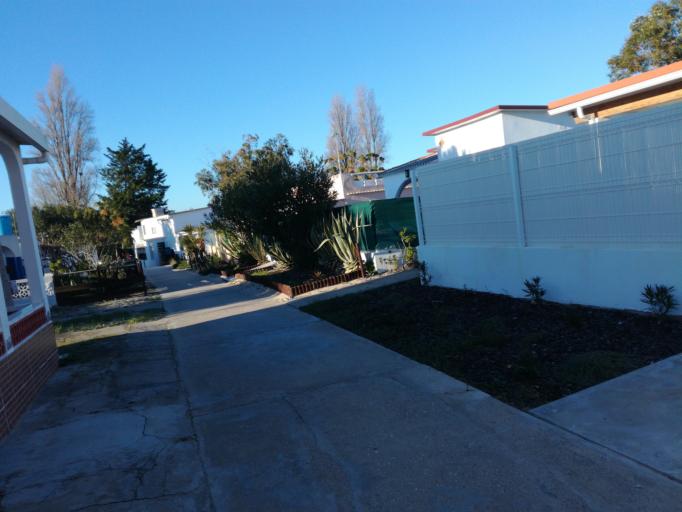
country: PT
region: Faro
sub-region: Olhao
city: Olhao
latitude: 37.0187
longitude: -7.8024
